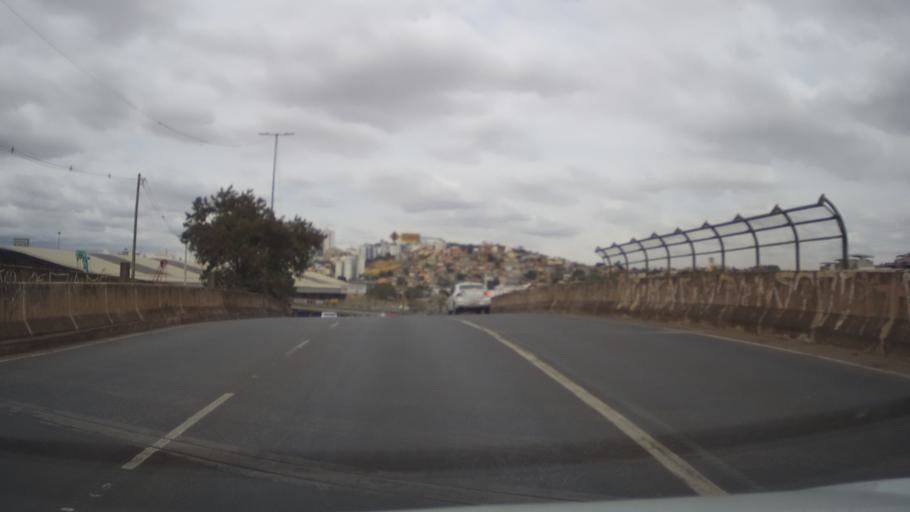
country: BR
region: Minas Gerais
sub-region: Belo Horizonte
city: Belo Horizonte
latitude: -19.8615
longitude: -43.9263
